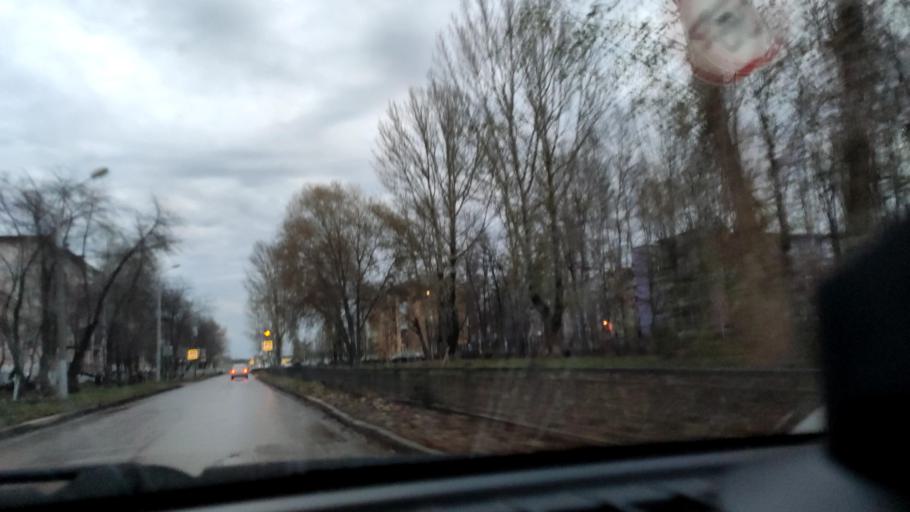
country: RU
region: Perm
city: Perm
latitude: 57.9949
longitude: 56.2991
